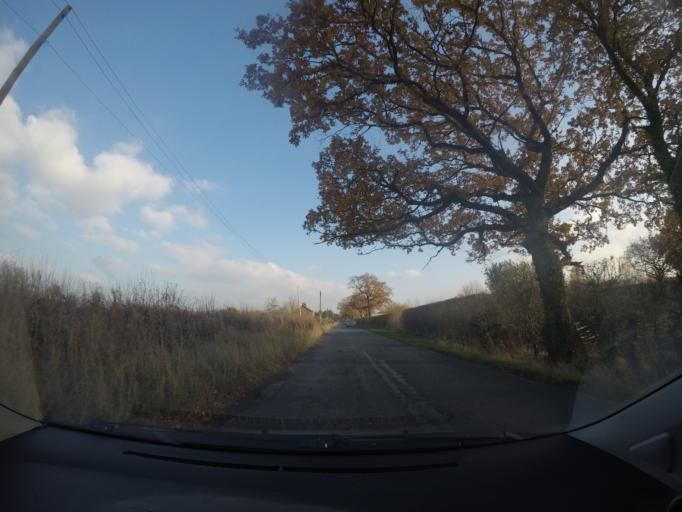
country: GB
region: England
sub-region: City of York
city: Huntington
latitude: 53.9995
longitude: -1.0328
